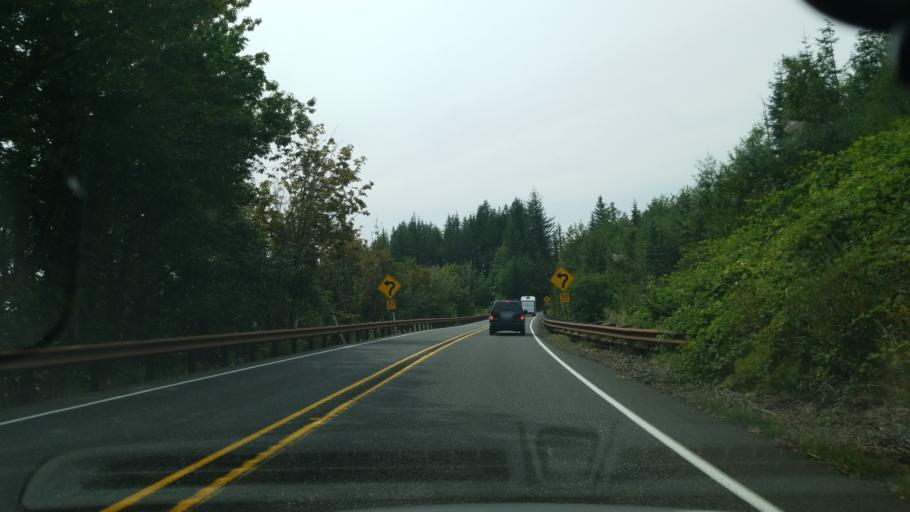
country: US
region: Washington
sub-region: Clark County
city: Washougal
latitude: 45.5661
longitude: -122.2137
